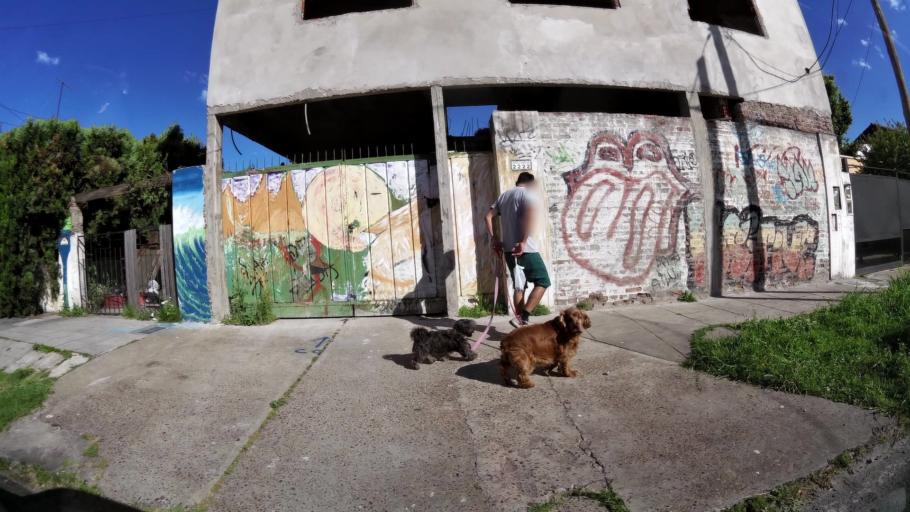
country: AR
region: Buenos Aires
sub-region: Partido de General San Martin
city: General San Martin
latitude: -34.5357
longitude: -58.5627
